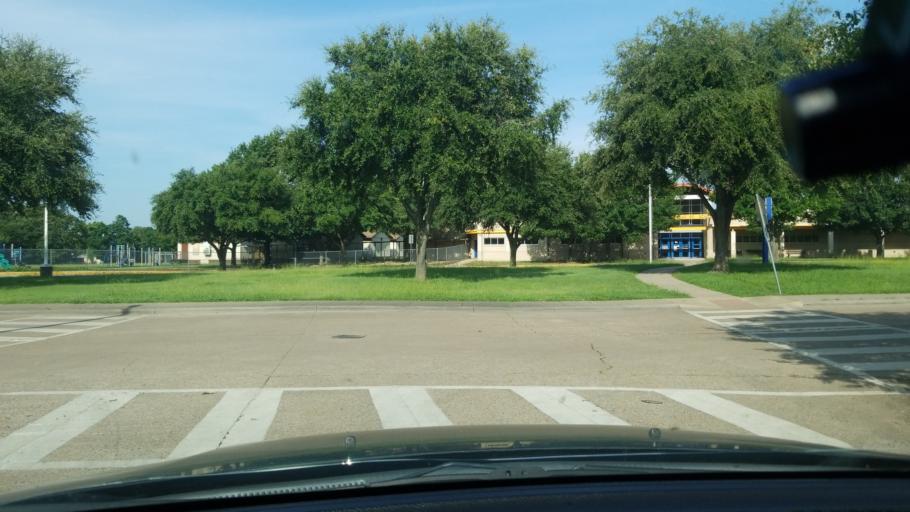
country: US
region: Texas
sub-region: Dallas County
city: Balch Springs
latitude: 32.7171
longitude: -96.6418
